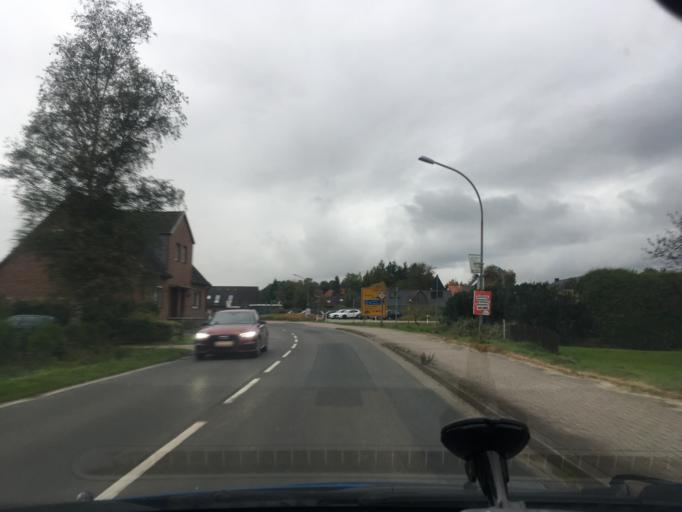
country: DE
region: Lower Saxony
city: Marschacht
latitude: 53.4188
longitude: 10.3424
